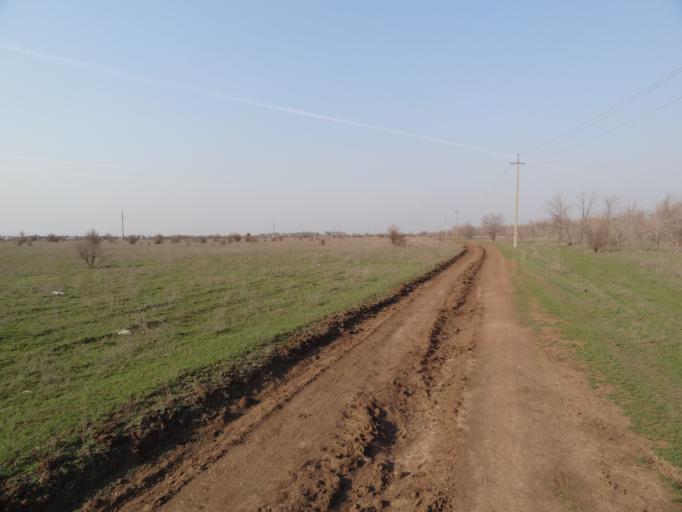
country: RU
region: Saratov
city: Privolzhskiy
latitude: 51.3245
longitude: 46.0278
